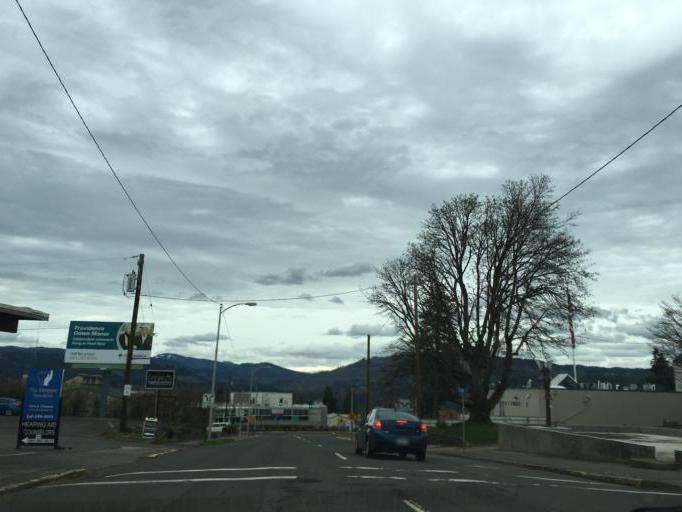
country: US
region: Oregon
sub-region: Hood River County
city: Hood River
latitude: 45.7031
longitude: -121.5237
